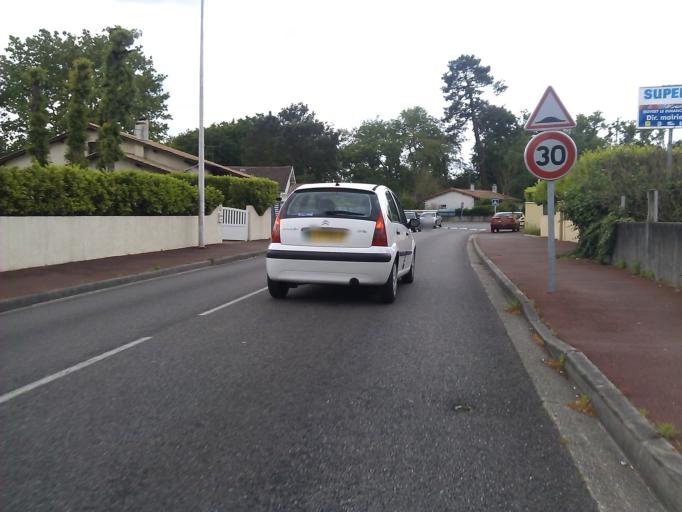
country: FR
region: Aquitaine
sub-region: Departement de la Gironde
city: Cestas
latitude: 44.7445
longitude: -0.6849
